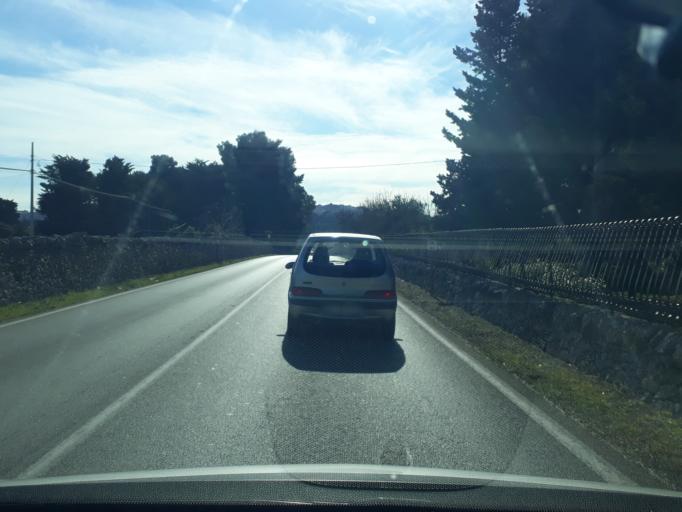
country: IT
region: Apulia
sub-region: Provincia di Taranto
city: Martina Franca
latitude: 40.7232
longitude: 17.3327
